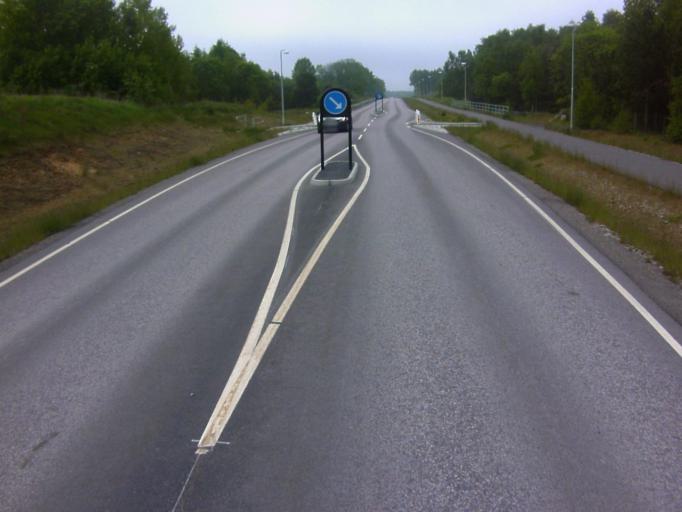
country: SE
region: Blekinge
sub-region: Solvesborgs Kommun
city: Soelvesborg
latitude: 56.0554
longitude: 14.6169
